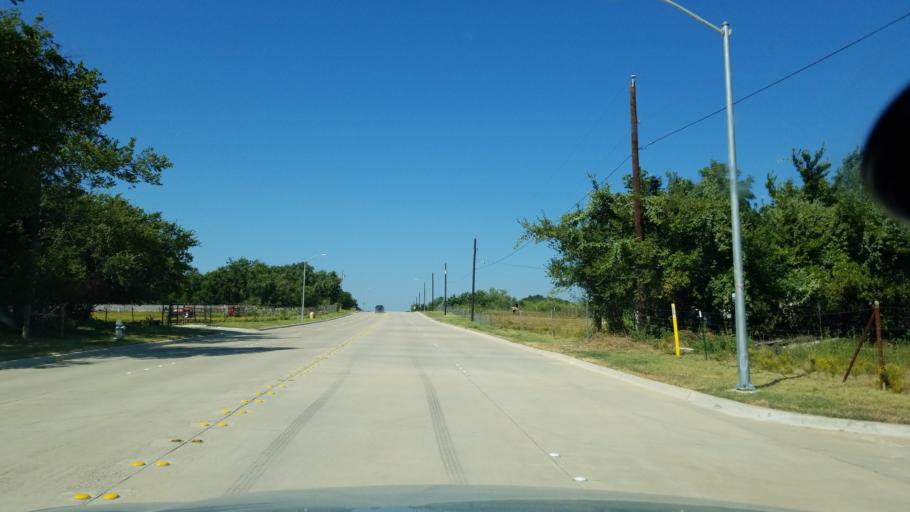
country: US
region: Texas
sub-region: Tarrant County
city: Mansfield
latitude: 32.5835
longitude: -97.1421
